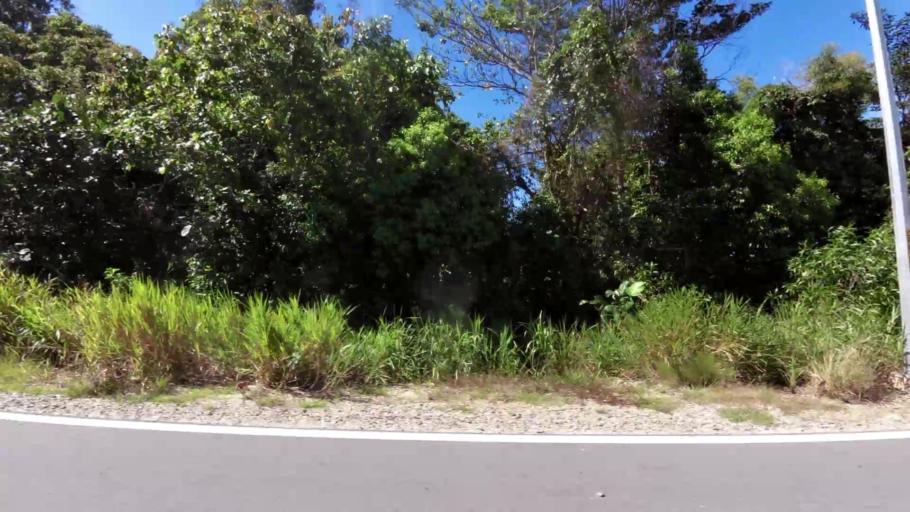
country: BN
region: Brunei and Muara
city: Bandar Seri Begawan
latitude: 5.0048
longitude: 115.0562
